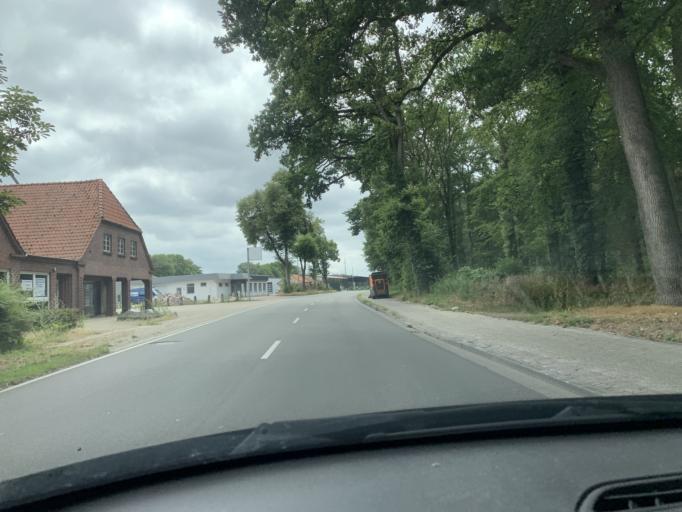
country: DE
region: Lower Saxony
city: Westerstede
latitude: 53.2697
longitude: 7.9400
